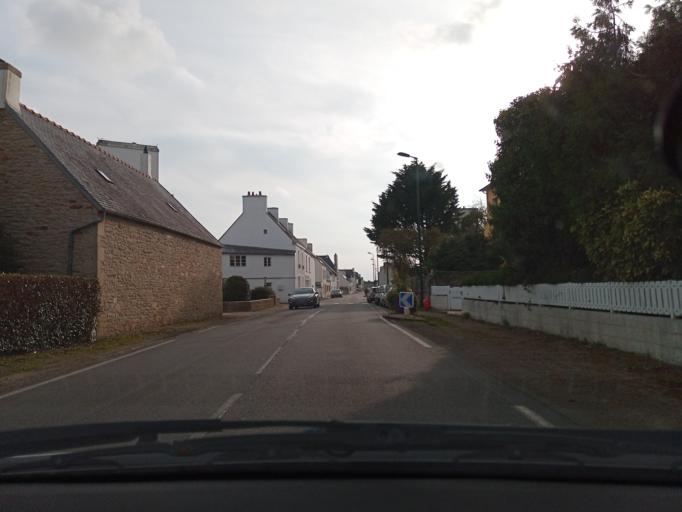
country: FR
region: Brittany
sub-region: Departement du Finistere
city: Plozevet
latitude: 47.9905
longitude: -4.4215
